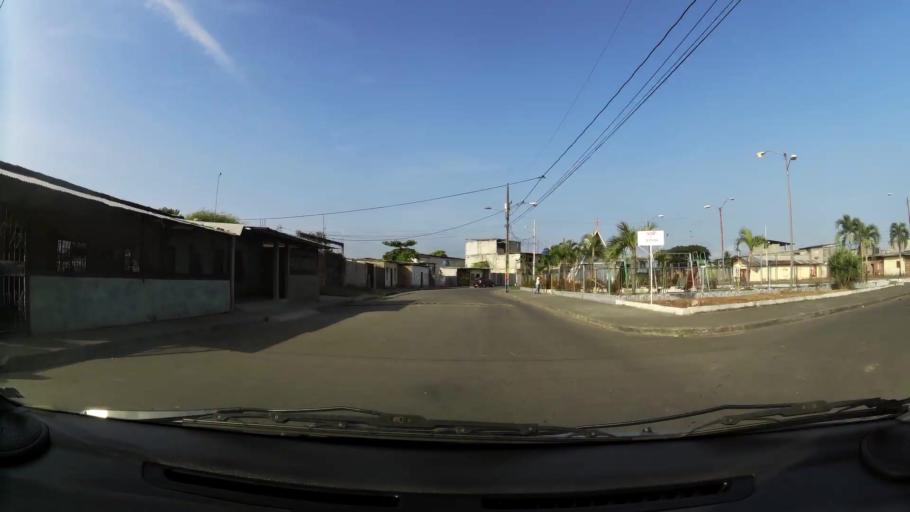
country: EC
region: Guayas
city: Eloy Alfaro
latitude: -2.1851
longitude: -79.8393
